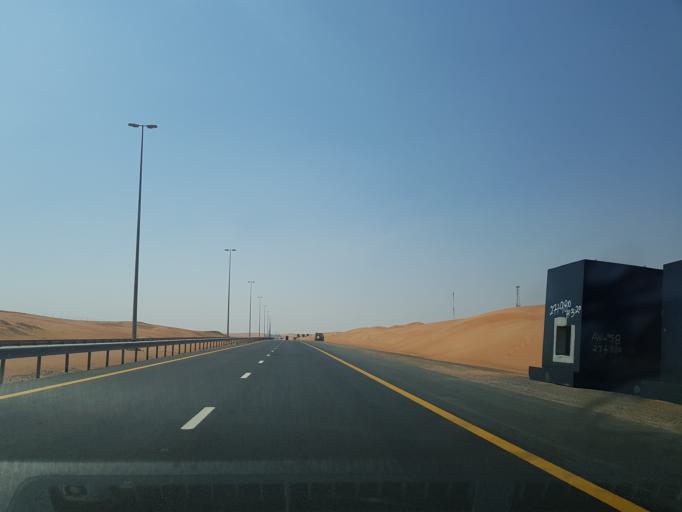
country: AE
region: Ash Shariqah
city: Adh Dhayd
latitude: 25.2473
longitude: 55.8391
